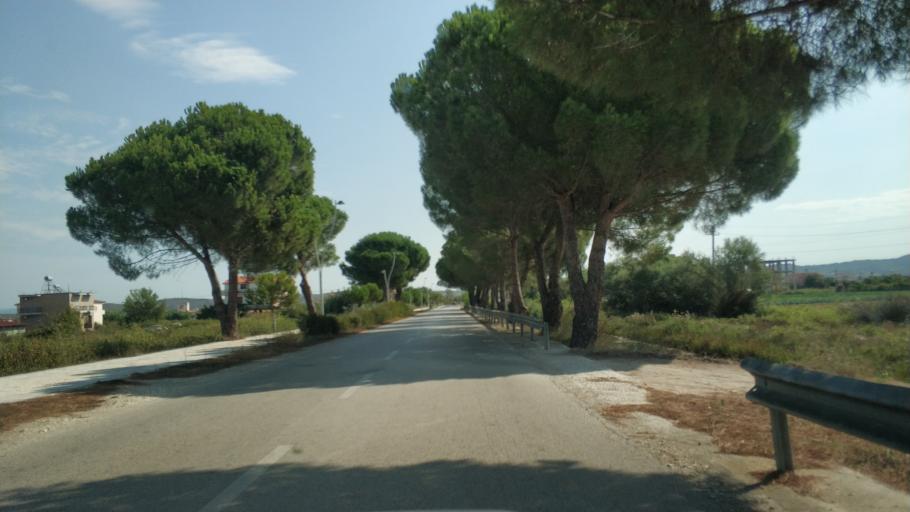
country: AL
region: Fier
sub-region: Rrethi i Lushnjes
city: Divjake
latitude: 40.9922
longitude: 19.5159
